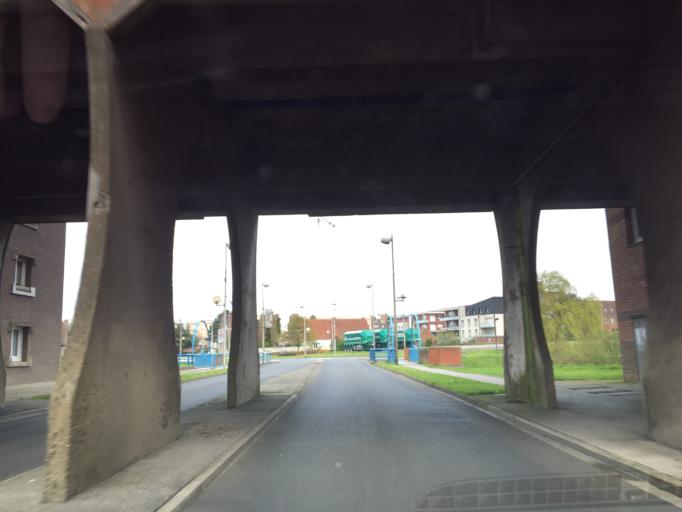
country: FR
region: Nord-Pas-de-Calais
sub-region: Departement du Nord
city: Grande-Synthe
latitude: 51.0113
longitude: 2.3016
